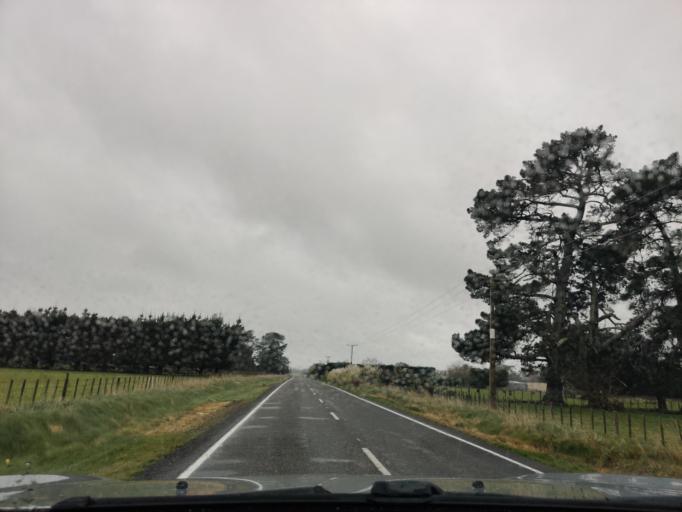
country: NZ
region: Hawke's Bay
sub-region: Hastings District
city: Hastings
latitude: -40.0194
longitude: 176.3428
